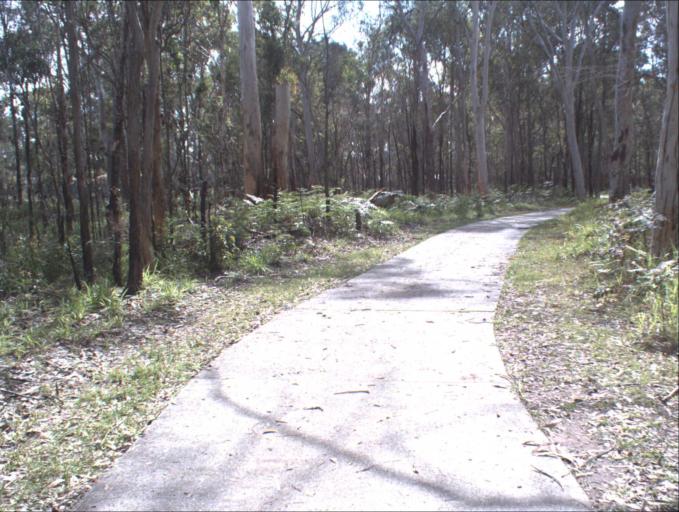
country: AU
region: Queensland
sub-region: Logan
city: Woodridge
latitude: -27.6732
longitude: 153.0569
